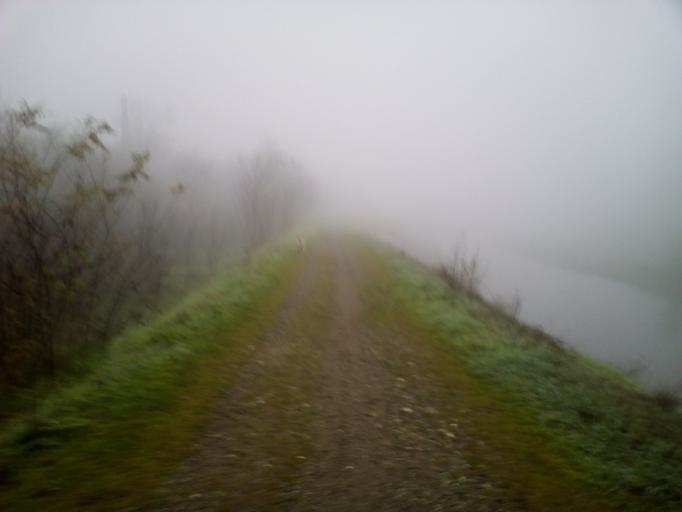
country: IT
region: Lombardy
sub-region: Provincia di Brescia
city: Roncadelle
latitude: 45.5209
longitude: 10.1543
